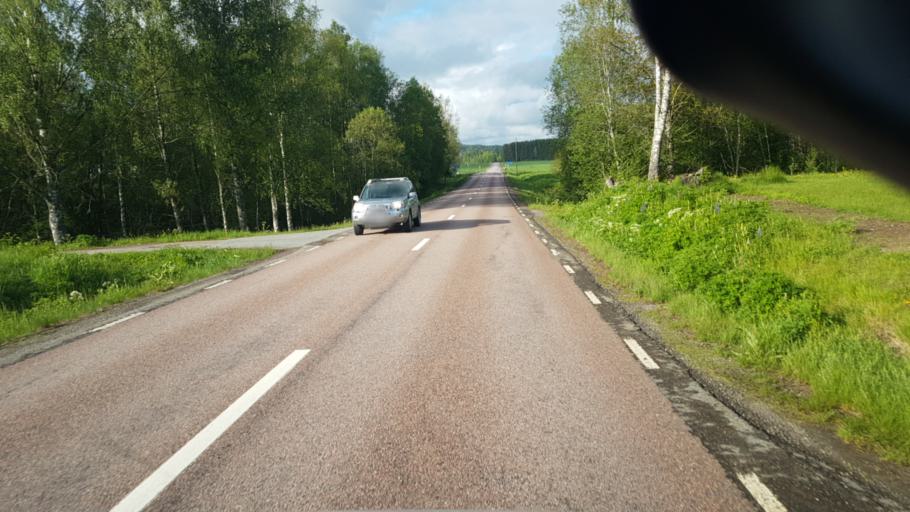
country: SE
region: Vaermland
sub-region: Eda Kommun
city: Amotfors
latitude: 59.7393
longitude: 12.2035
